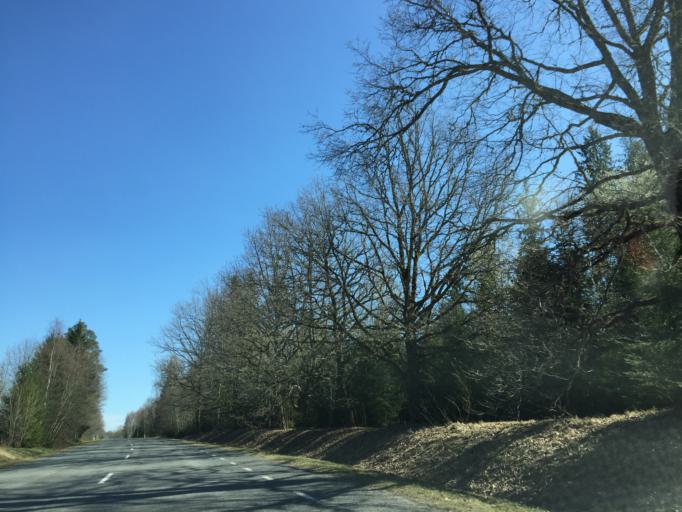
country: EE
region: Viljandimaa
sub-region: Viljandi linn
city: Viljandi
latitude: 58.2785
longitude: 25.5970
